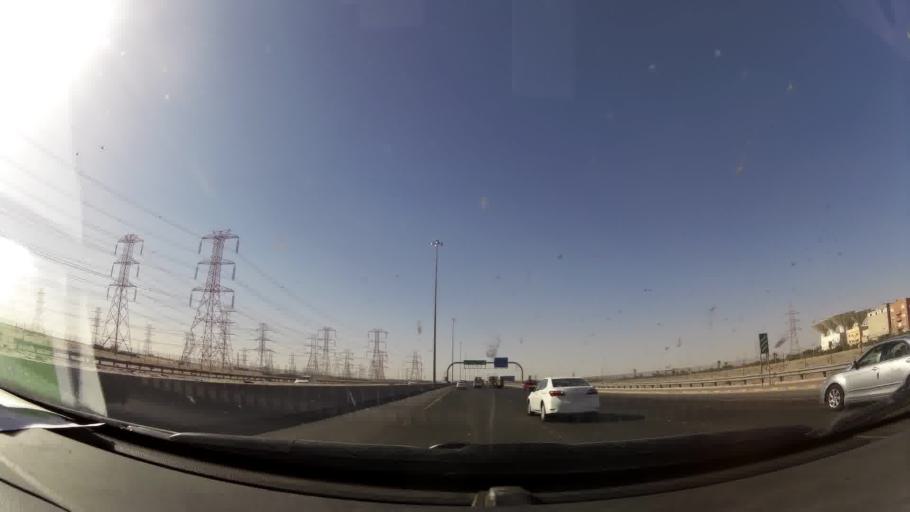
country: KW
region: Muhafazat al Jahra'
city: Al Jahra'
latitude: 29.3014
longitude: 47.6875
